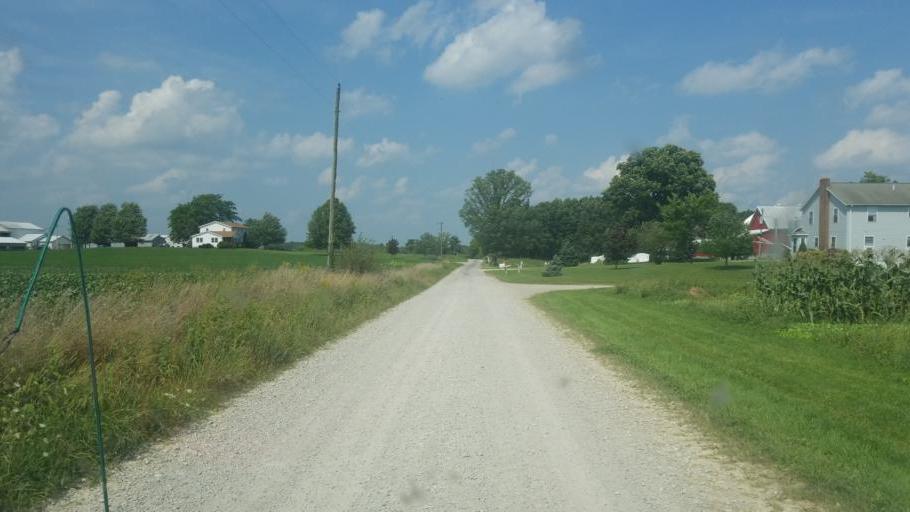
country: US
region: Ohio
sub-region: Huron County
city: New London
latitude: 40.9778
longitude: -82.4080
